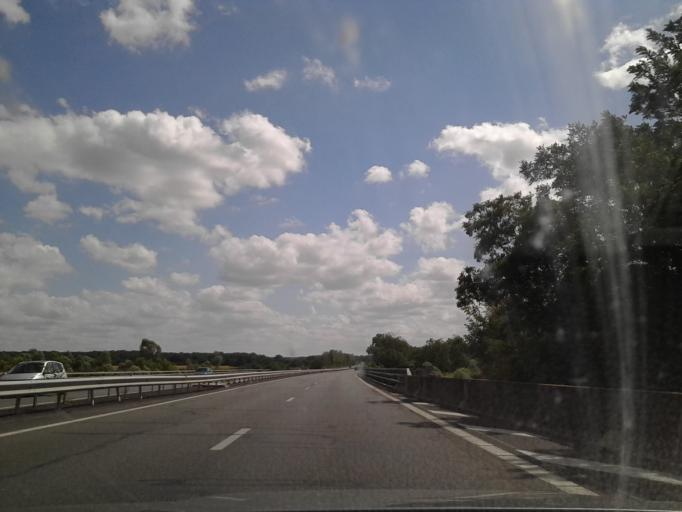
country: FR
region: Centre
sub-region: Departement du Cher
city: Orval
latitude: 46.7844
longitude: 2.4114
